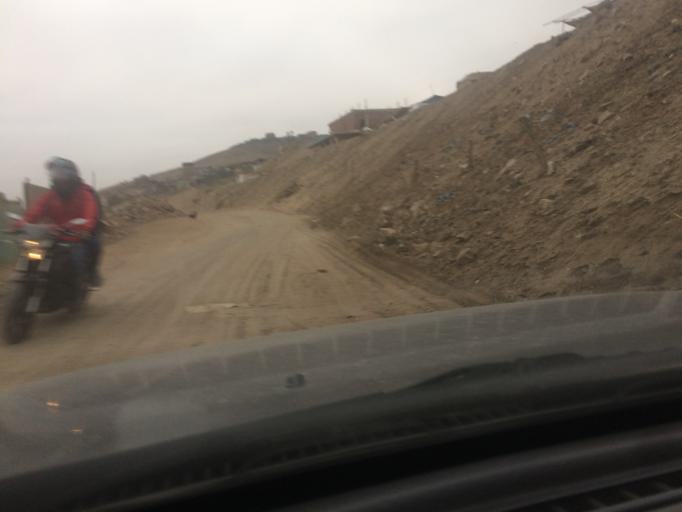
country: PE
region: Lima
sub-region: Lima
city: Cieneguilla
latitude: -12.2224
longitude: -76.8866
